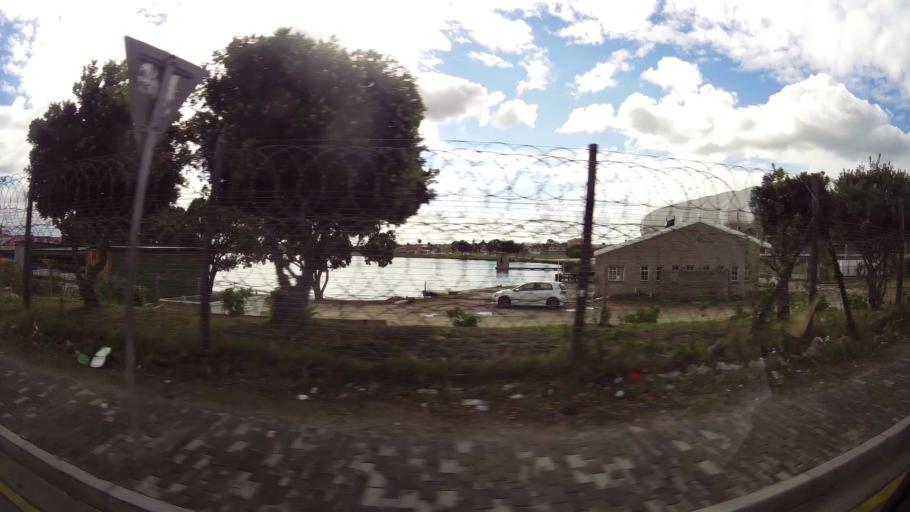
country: ZA
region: Eastern Cape
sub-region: Nelson Mandela Bay Metropolitan Municipality
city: Port Elizabeth
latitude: -33.9391
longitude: 25.5967
